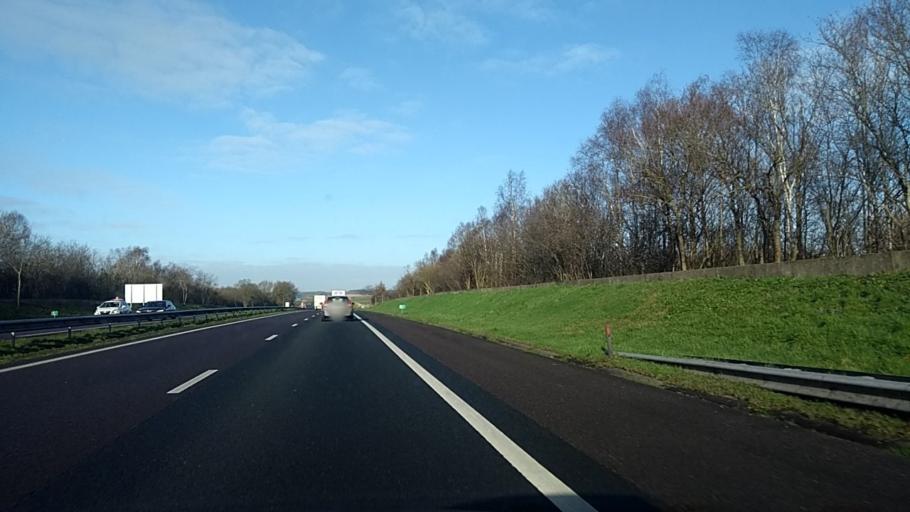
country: NL
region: Overijssel
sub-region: Gemeente Steenwijkerland
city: Steenwijk
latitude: 52.7887
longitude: 6.1569
